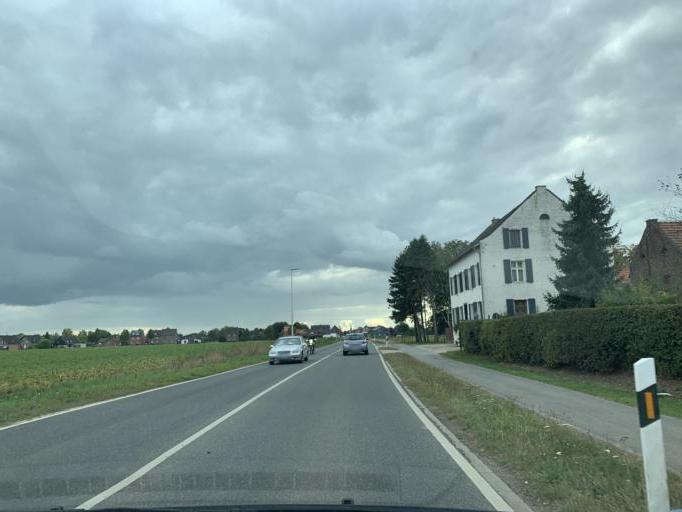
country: DE
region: North Rhine-Westphalia
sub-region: Regierungsbezirk Koln
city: Wassenberg
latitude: 51.0797
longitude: 6.1401
